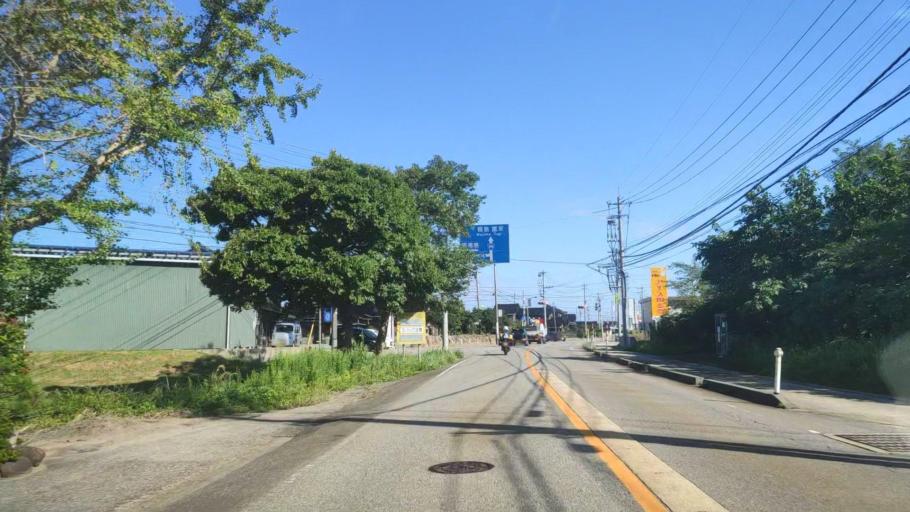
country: JP
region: Ishikawa
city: Hakui
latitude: 36.9954
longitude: 136.7767
